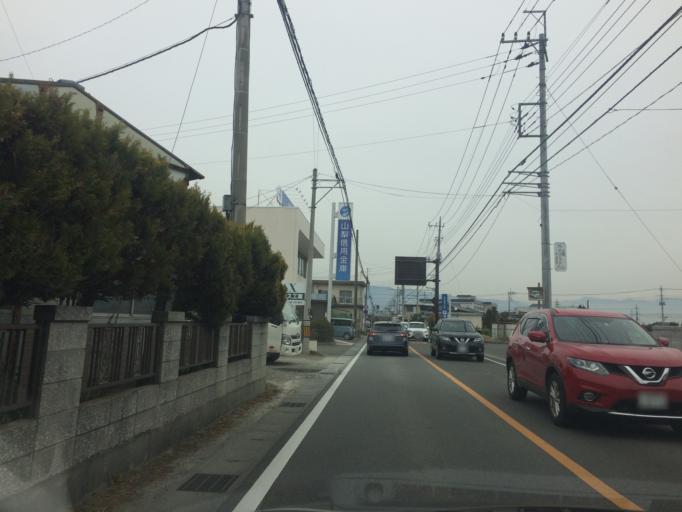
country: JP
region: Yamanashi
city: Ryuo
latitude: 35.6197
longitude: 138.5330
